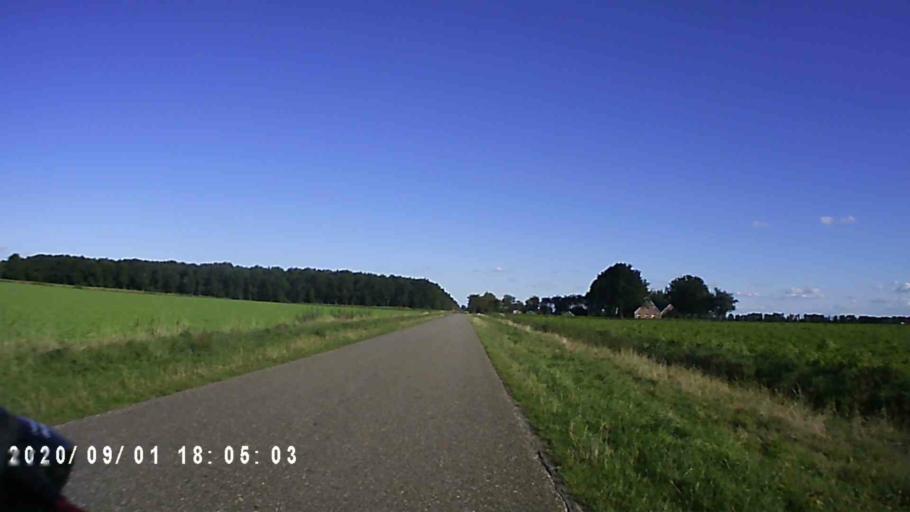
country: NL
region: Groningen
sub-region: Gemeente Slochteren
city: Slochteren
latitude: 53.1990
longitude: 6.7935
